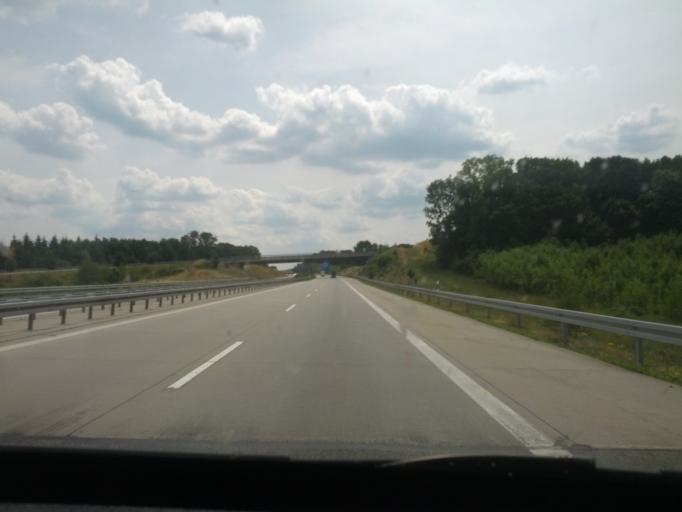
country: DE
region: Saxony
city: Liebstadt
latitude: 50.8432
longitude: 13.8817
